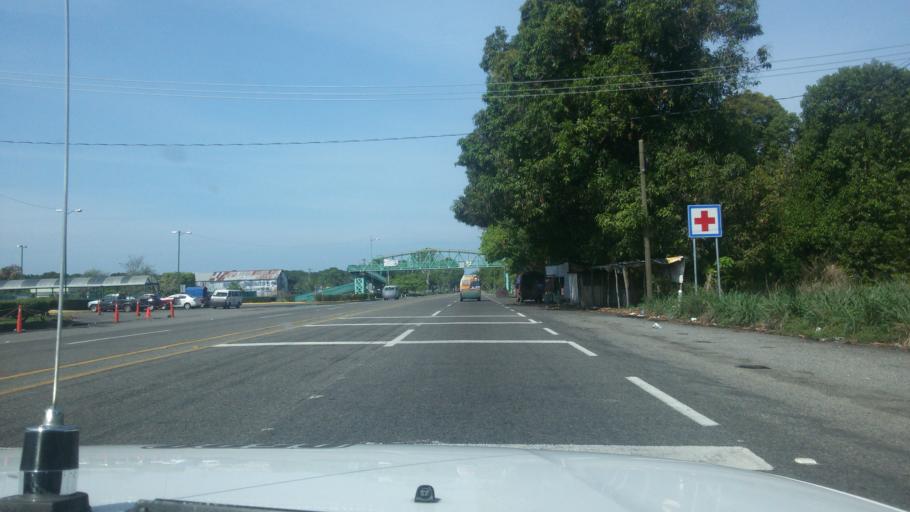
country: MX
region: Chiapas
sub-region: Tapachula
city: Congregacion Reforma
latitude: 14.8109
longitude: -92.3463
